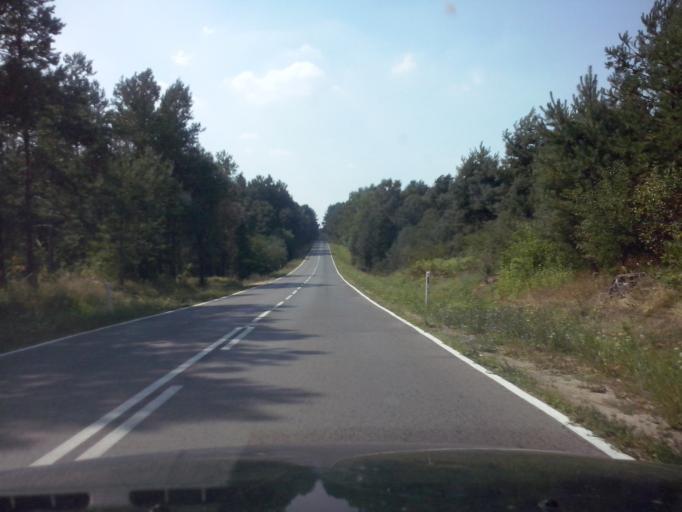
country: PL
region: Swietokrzyskie
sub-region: Powiat staszowski
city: Szydlow
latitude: 50.6266
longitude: 21.0234
